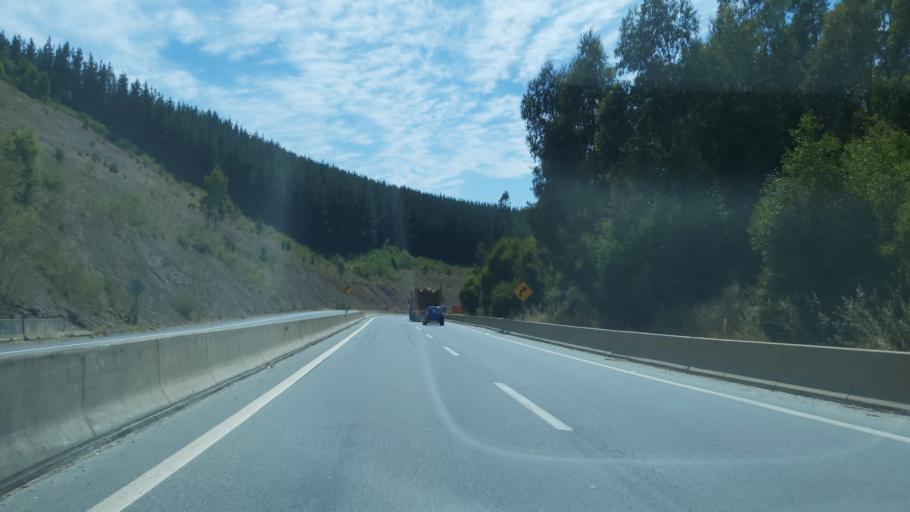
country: CL
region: Biobio
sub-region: Provincia de Concepcion
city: Lota
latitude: -37.1019
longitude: -73.1466
